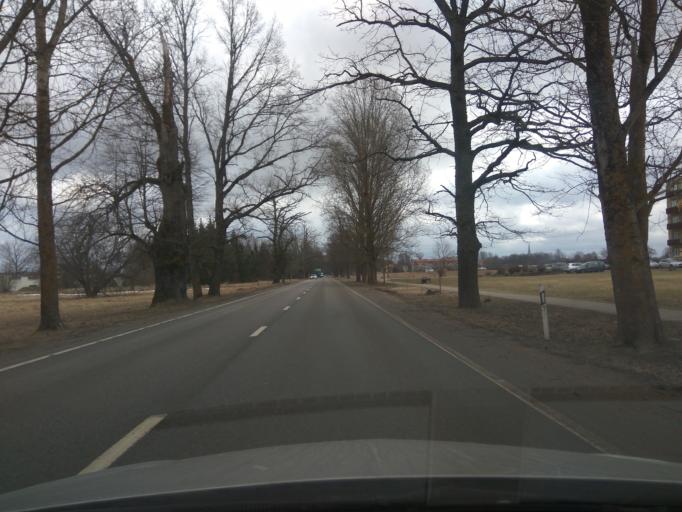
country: LV
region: Kuldigas Rajons
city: Kuldiga
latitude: 57.2760
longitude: 22.0258
